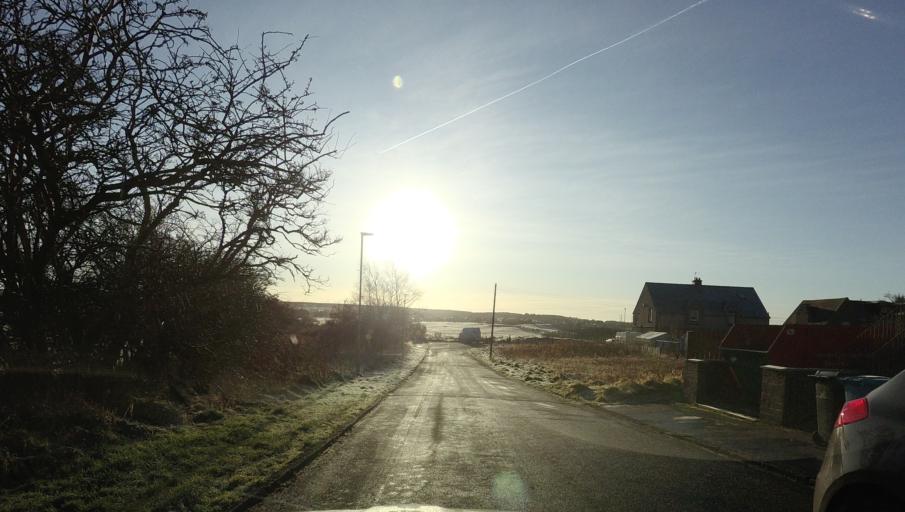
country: GB
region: Scotland
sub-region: North Lanarkshire
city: Shotts
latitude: 55.8104
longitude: -3.8362
